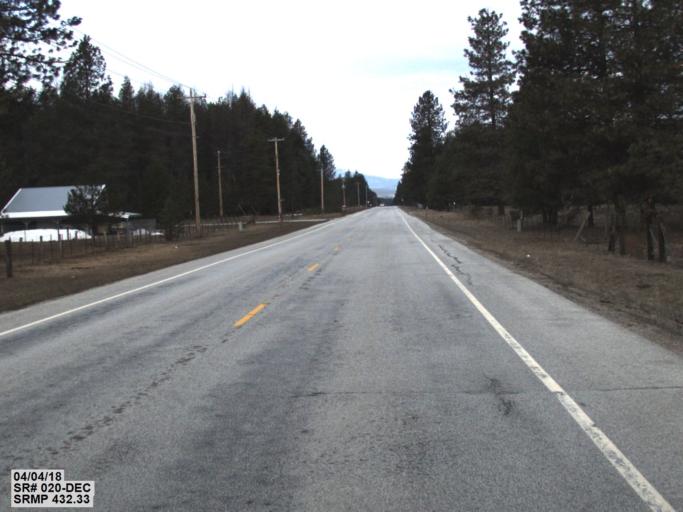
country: US
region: Washington
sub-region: Pend Oreille County
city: Newport
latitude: 48.2222
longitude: -117.1130
